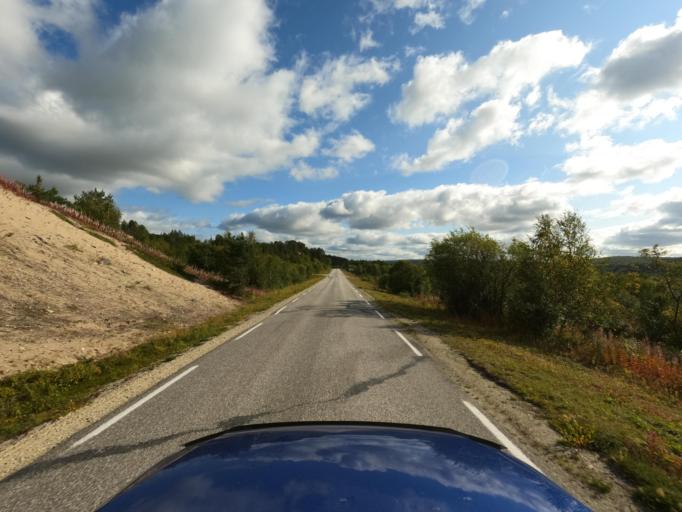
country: NO
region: Finnmark Fylke
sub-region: Karasjok
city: Karasjohka
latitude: 69.4438
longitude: 25.2229
